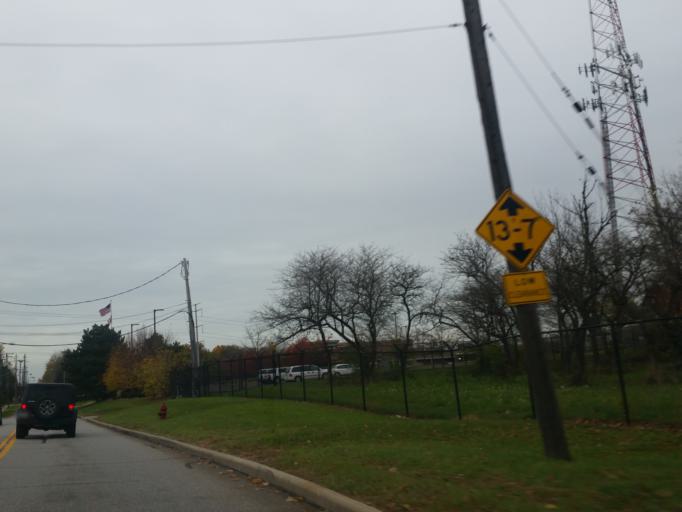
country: US
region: Ohio
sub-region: Cuyahoga County
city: Newburgh Heights
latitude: 41.4280
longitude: -81.6565
